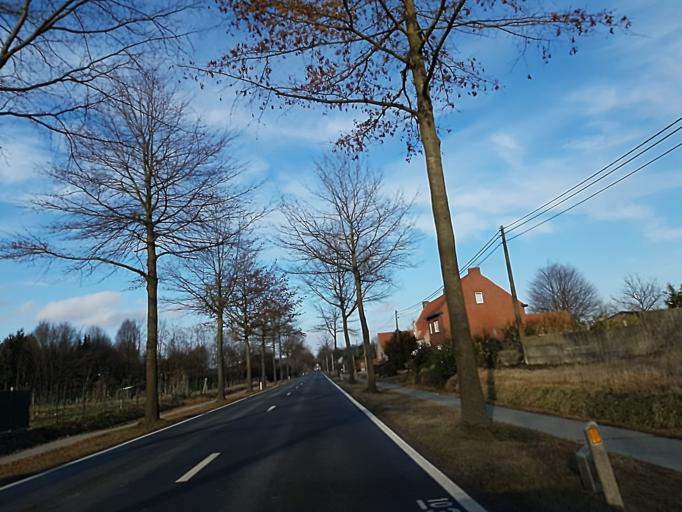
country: BE
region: Flanders
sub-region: Provincie Antwerpen
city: Retie
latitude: 51.2425
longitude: 5.0708
